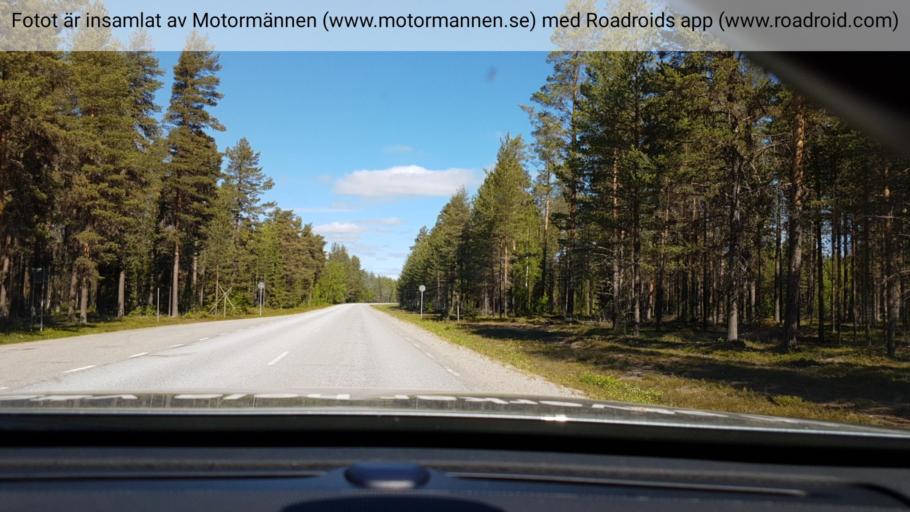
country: SE
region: Vaesterbotten
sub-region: Asele Kommun
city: Asele
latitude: 64.1753
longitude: 17.3593
